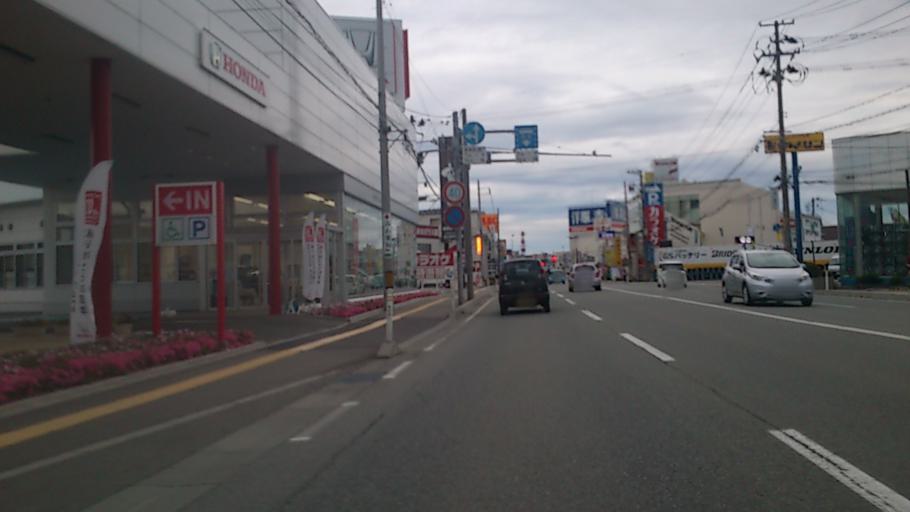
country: JP
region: Akita
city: Akita Shi
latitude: 39.7304
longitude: 140.1035
